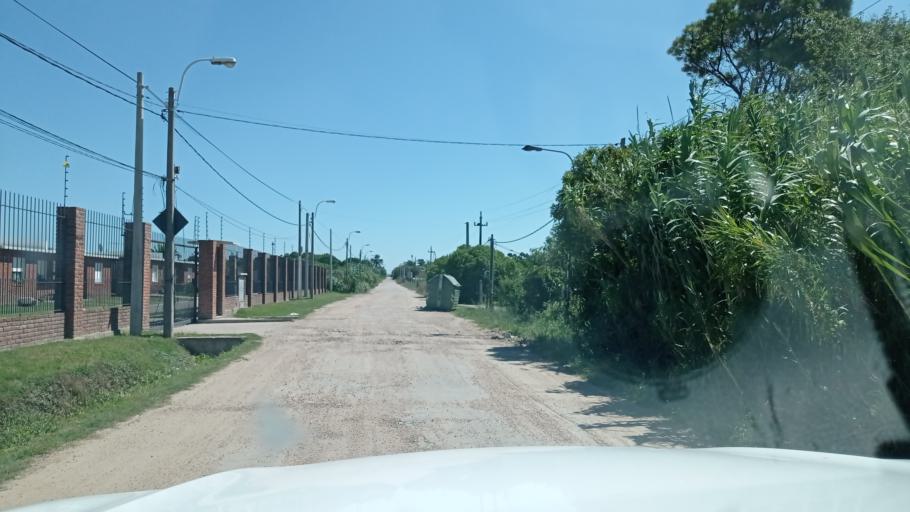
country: UY
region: Montevideo
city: Montevideo
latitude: -34.8691
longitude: -56.2727
